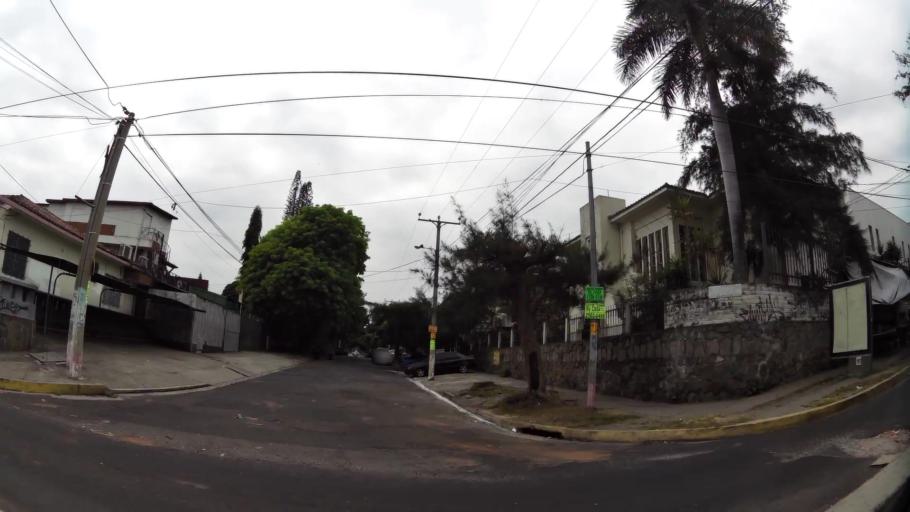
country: SV
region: San Salvador
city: San Salvador
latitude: 13.7025
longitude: -89.2170
